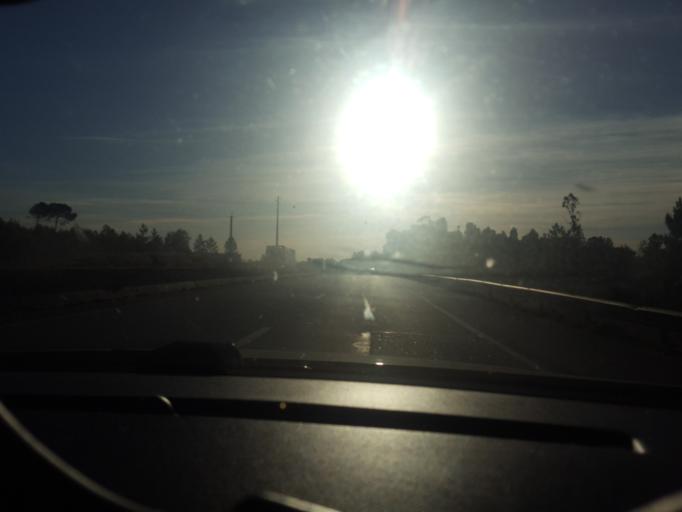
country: PT
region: Viseu
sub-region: Concelho de Carregal do Sal
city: Carregal do Sal
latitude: 40.4620
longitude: -7.9582
